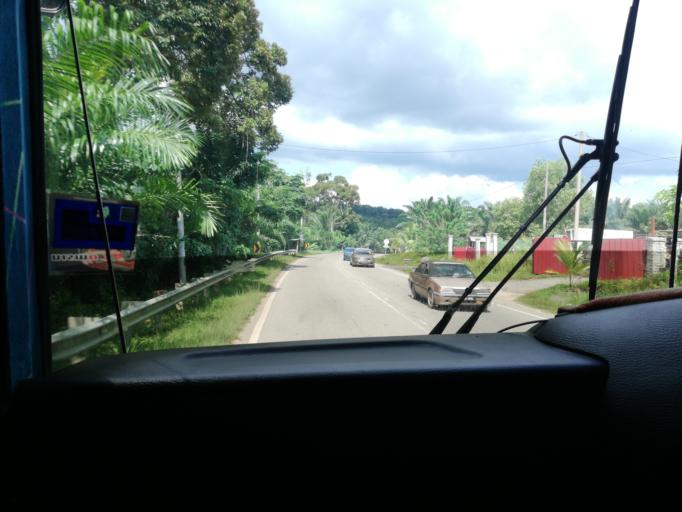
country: MY
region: Perak
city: Parit Buntar
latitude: 5.1282
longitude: 100.5713
